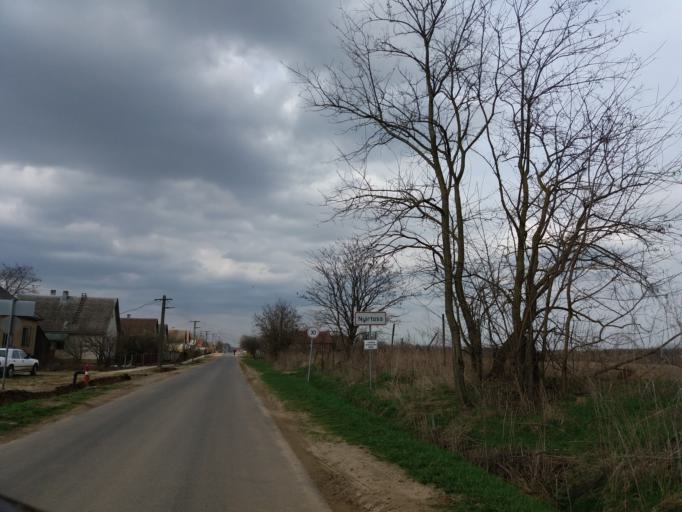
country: HU
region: Szabolcs-Szatmar-Bereg
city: Nyirtass
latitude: 48.0990
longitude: 22.0289
